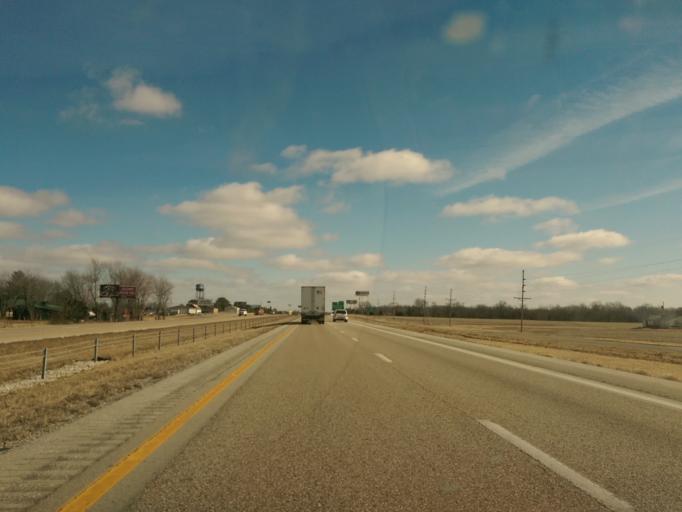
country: US
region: Missouri
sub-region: Montgomery County
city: Montgomery City
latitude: 38.9030
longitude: -91.4787
